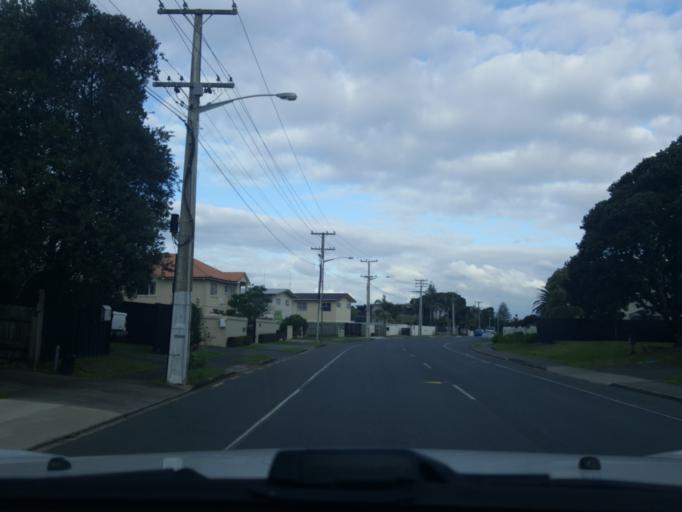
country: NZ
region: Bay of Plenty
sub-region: Tauranga City
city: Tauranga
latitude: -37.6556
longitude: 176.2092
